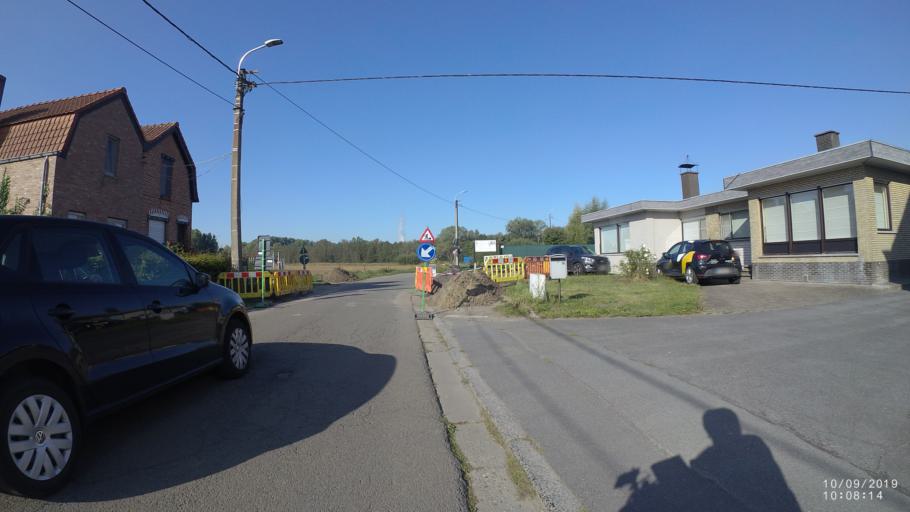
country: BE
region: Flanders
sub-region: Provincie Oost-Vlaanderen
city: Zelzate
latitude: 51.1443
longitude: 3.8169
